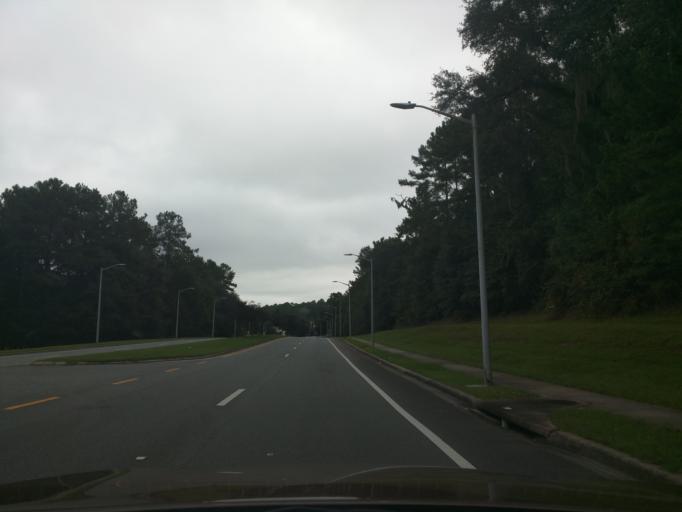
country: US
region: Florida
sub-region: Leon County
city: Tallahassee
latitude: 30.4318
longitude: -84.2019
